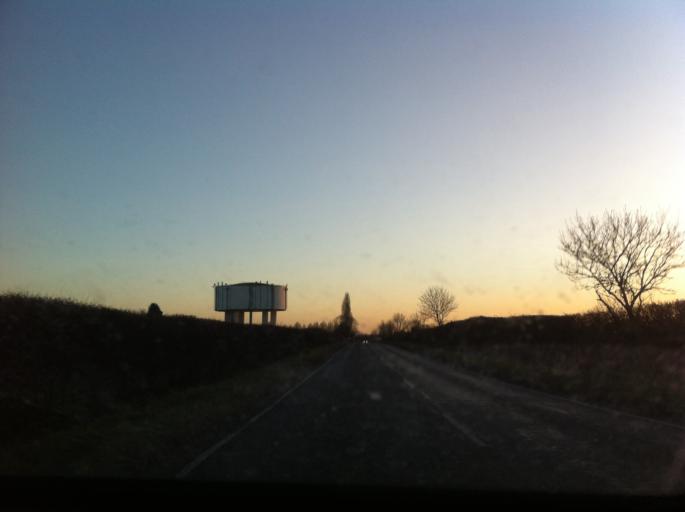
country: GB
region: England
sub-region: Northamptonshire
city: Irchester
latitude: 52.2610
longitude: -0.6584
